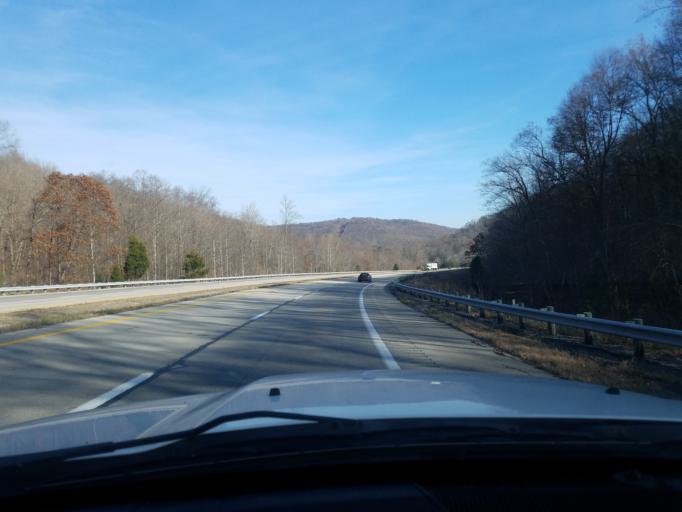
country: US
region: Ohio
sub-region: Adams County
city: Peebles
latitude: 39.0308
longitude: -83.2657
